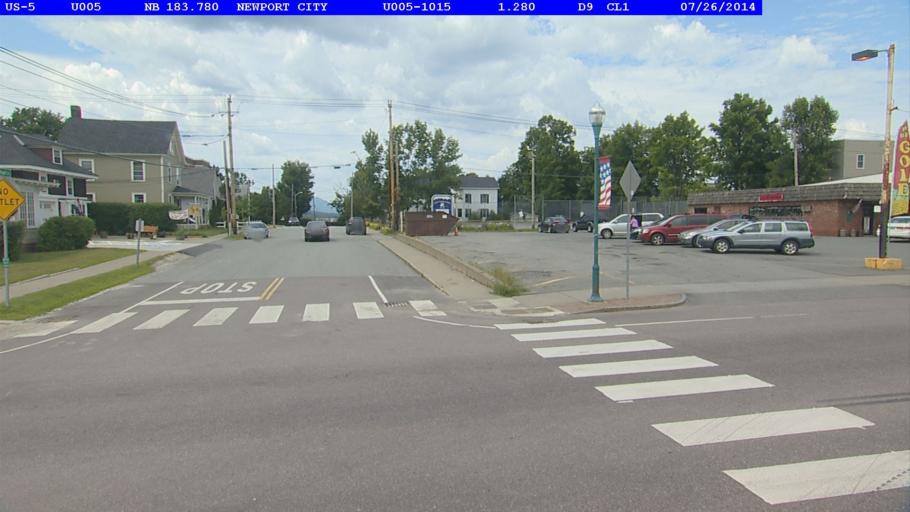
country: US
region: Vermont
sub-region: Orleans County
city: Newport
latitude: 44.9348
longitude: -72.2119
